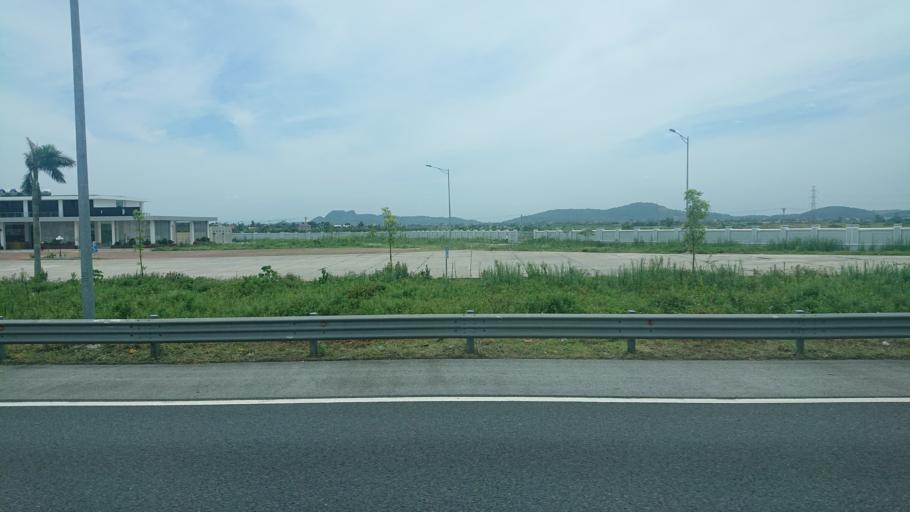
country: VN
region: Hai Phong
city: An Lao
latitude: 20.7929
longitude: 106.5492
